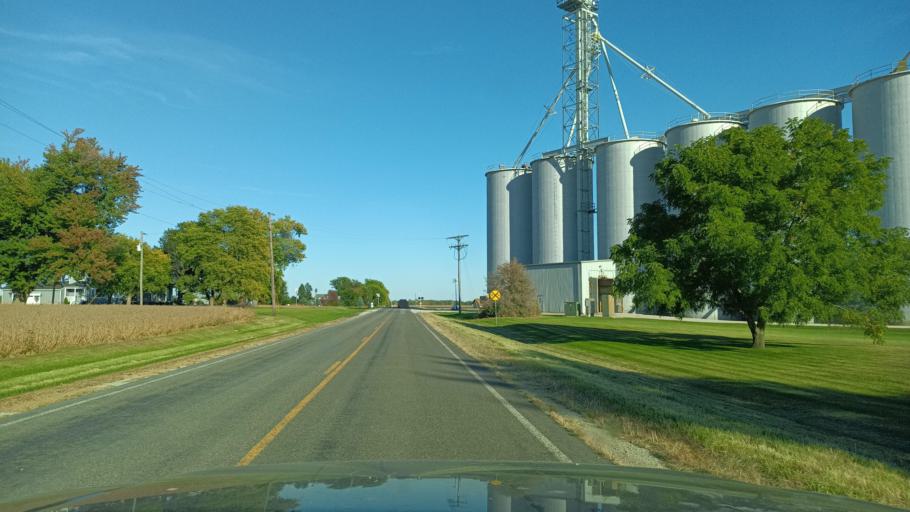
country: US
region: Illinois
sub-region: De Witt County
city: Farmer City
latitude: 40.2238
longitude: -88.7197
